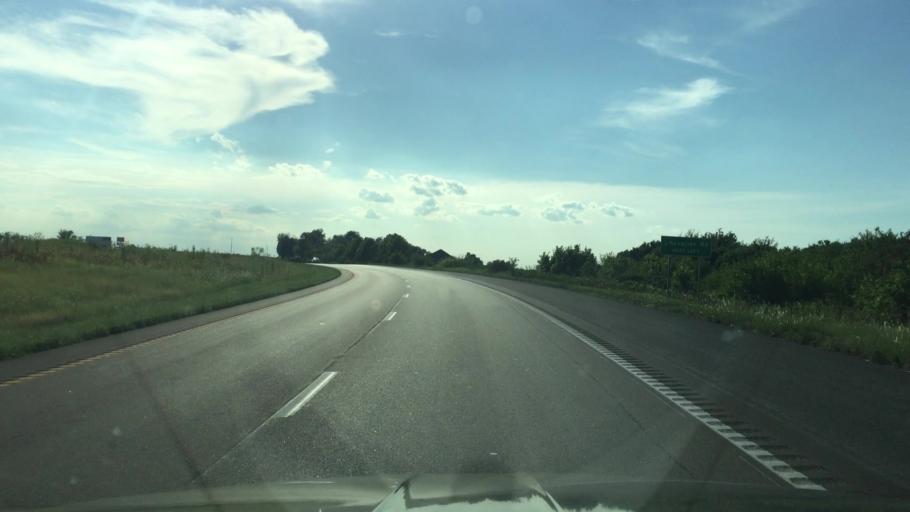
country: US
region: Missouri
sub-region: Pettis County
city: La Monte
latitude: 38.7614
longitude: -93.3759
